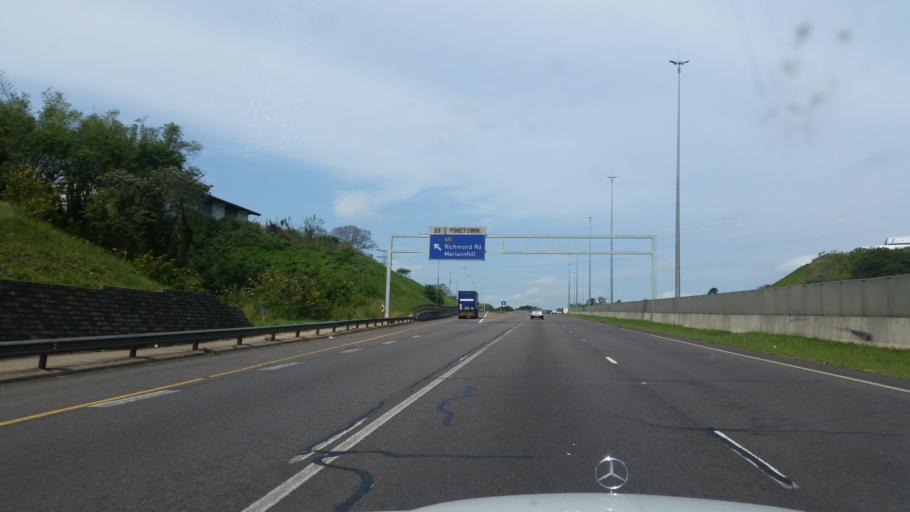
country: ZA
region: KwaZulu-Natal
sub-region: eThekwini Metropolitan Municipality
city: Berea
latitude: -29.8272
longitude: 30.8276
